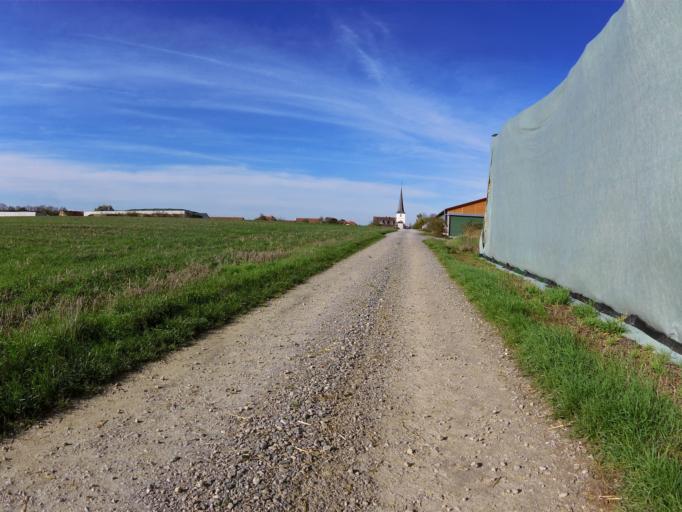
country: DE
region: Bavaria
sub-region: Regierungsbezirk Unterfranken
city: Biebelried
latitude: 49.7254
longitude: 10.0901
